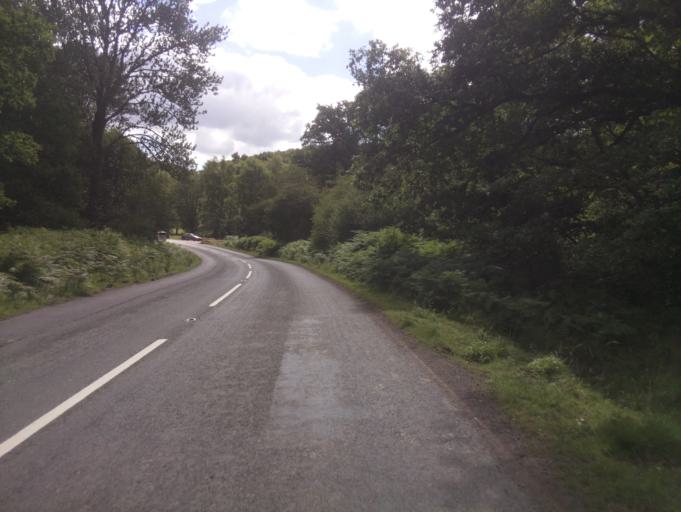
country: GB
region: England
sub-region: Gloucestershire
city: Lydney
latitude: 51.7773
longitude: -2.5281
